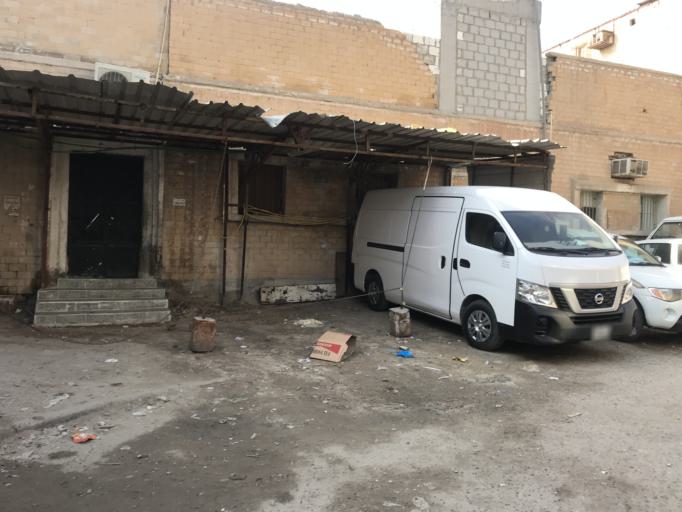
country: KW
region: Al Asimah
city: Ar Rabiyah
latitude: 29.2616
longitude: 47.9212
